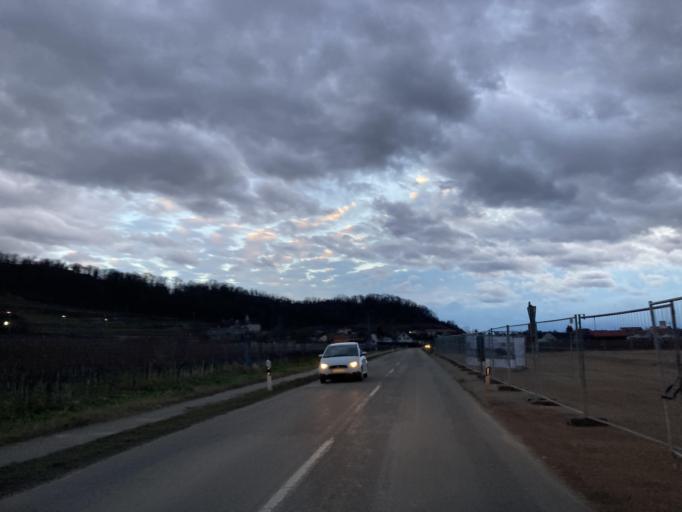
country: DE
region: Baden-Wuerttemberg
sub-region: Freiburg Region
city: Vogtsburg
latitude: 48.0896
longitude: 7.6199
